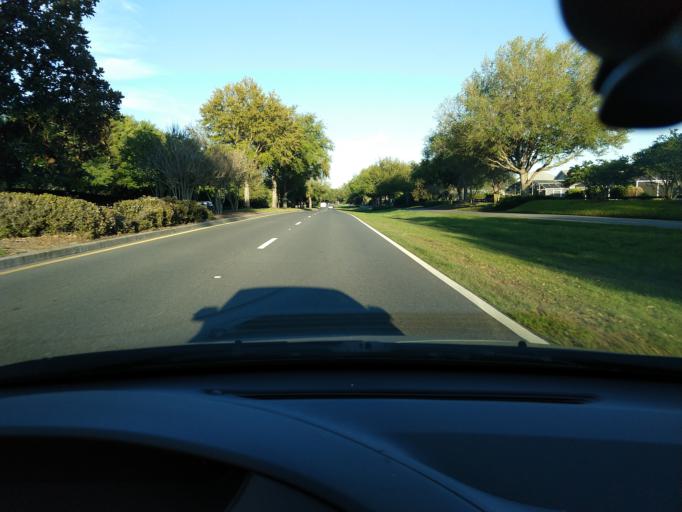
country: US
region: Florida
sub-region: Sumter County
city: The Villages
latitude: 28.9526
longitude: -81.9694
